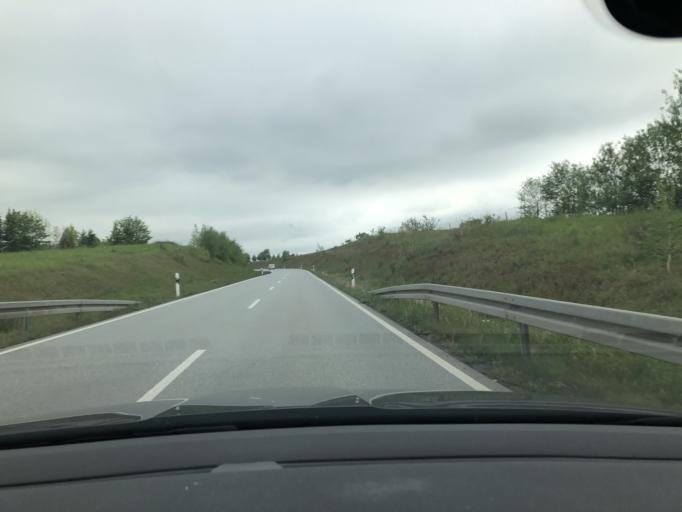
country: DE
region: Saxony
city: Dohma
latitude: 50.9011
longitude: 13.9112
